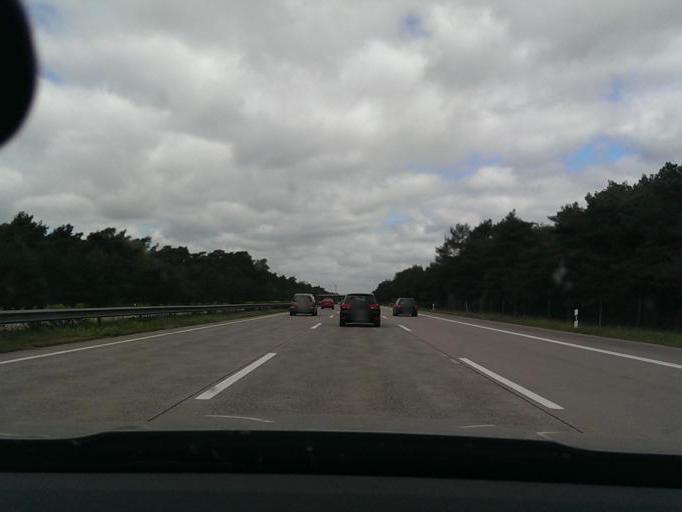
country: DE
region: Lower Saxony
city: Lindwedel
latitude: 52.6248
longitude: 9.7265
